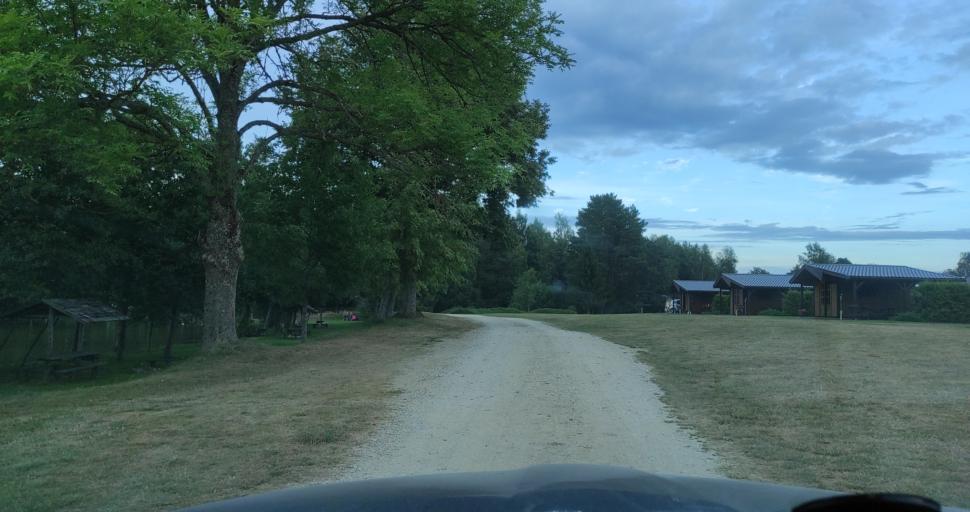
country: LV
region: Alsunga
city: Alsunga
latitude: 56.9332
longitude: 21.6465
